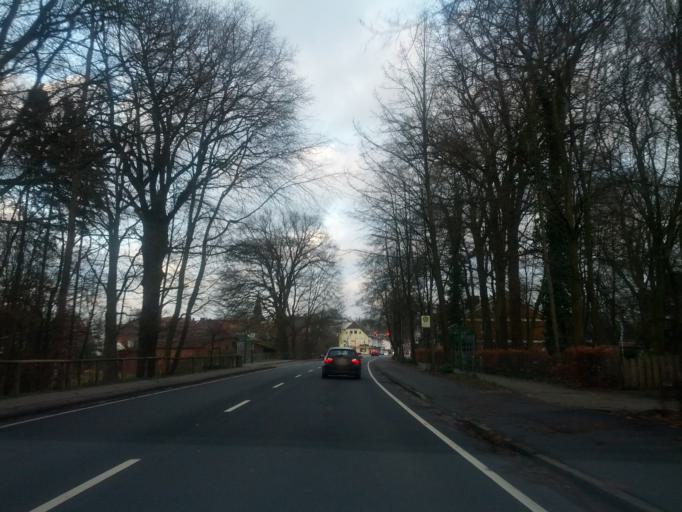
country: DE
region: Lower Saxony
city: Scheessel
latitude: 53.1663
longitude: 9.4793
